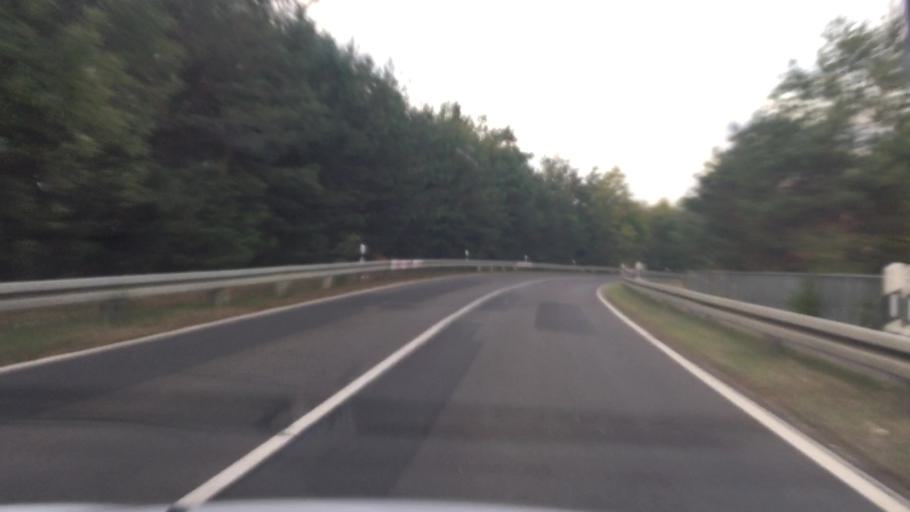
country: DE
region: Brandenburg
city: Schipkau
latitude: 51.4907
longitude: 13.8905
